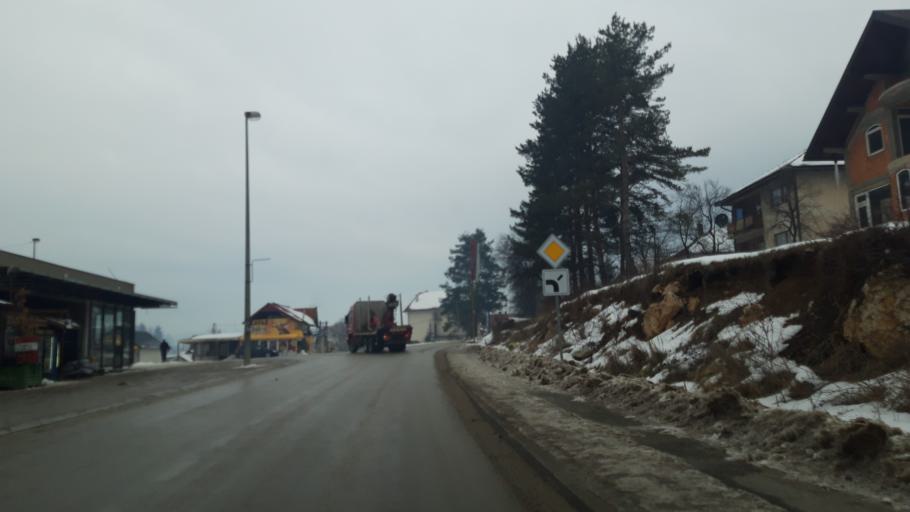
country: BA
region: Republika Srpska
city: Sokolac
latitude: 43.9381
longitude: 18.7992
